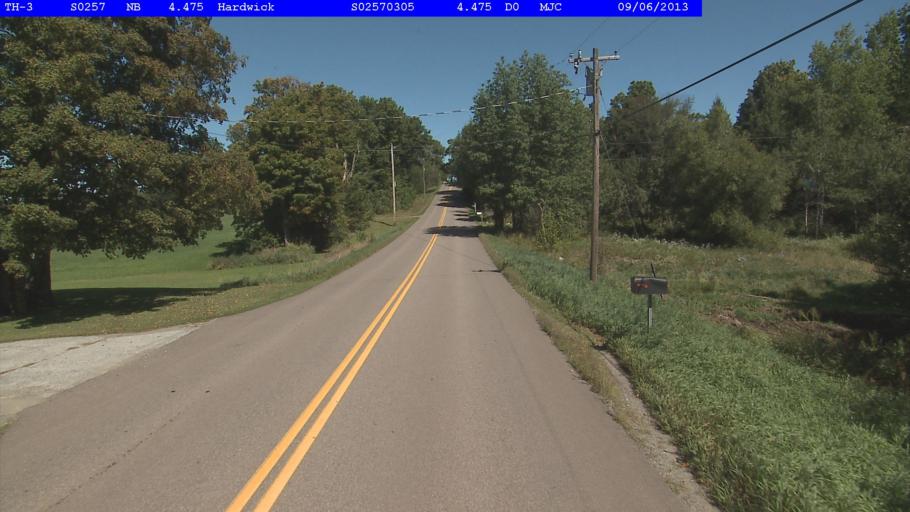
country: US
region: Vermont
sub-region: Caledonia County
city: Hardwick
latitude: 44.5518
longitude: -72.3191
